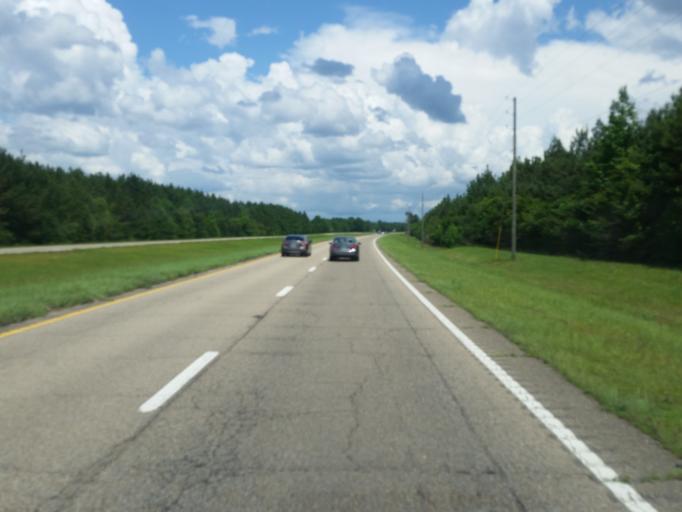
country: US
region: Mississippi
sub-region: Perry County
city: New Augusta
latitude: 31.1441
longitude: -88.8751
